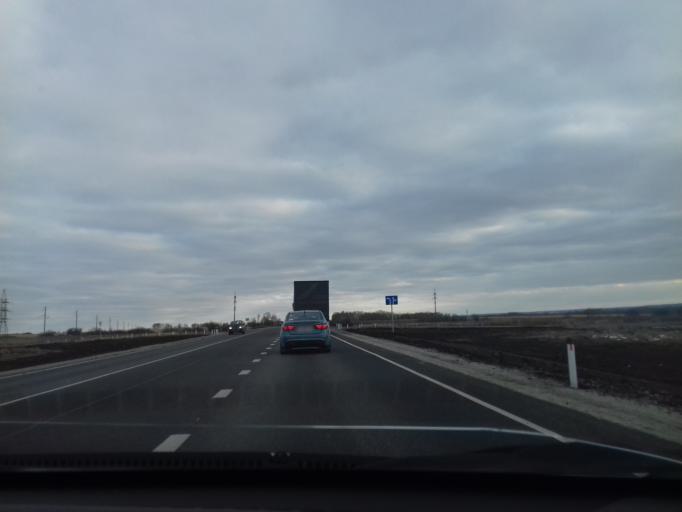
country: RU
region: Kurgan
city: Kataysk
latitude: 56.2939
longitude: 62.6716
